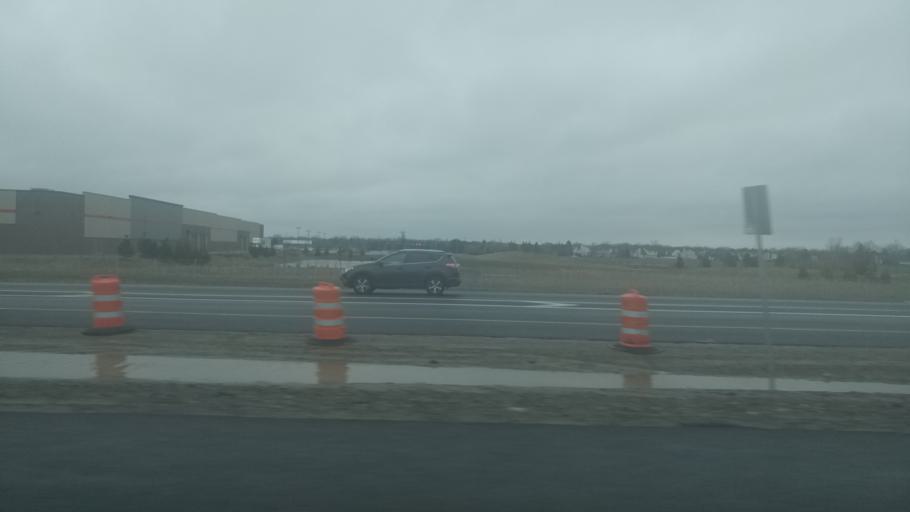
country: US
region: Ohio
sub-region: Wood County
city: Perrysburg
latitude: 41.5327
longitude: -83.6317
